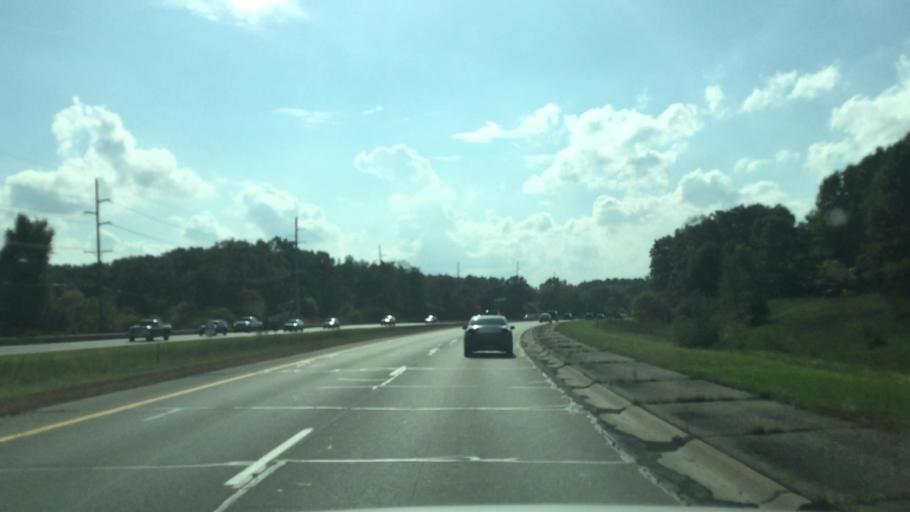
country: US
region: Michigan
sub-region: Oakland County
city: Milford
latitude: 42.6451
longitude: -83.5990
